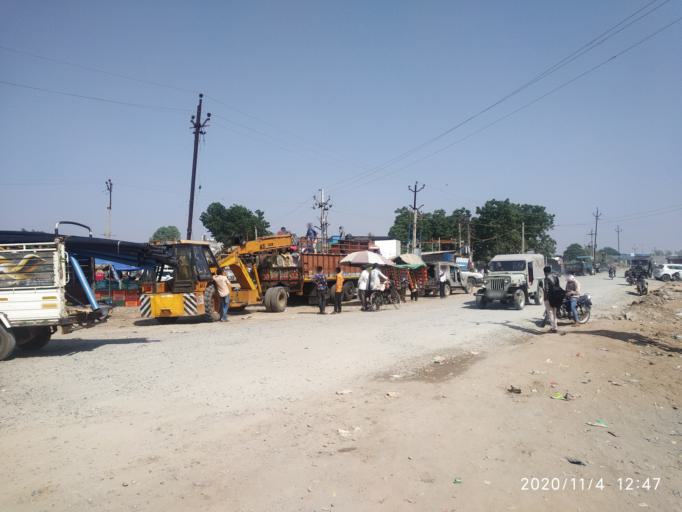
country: IN
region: Gujarat
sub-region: Banas Kantha
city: Tharad
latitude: 24.3979
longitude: 71.6388
